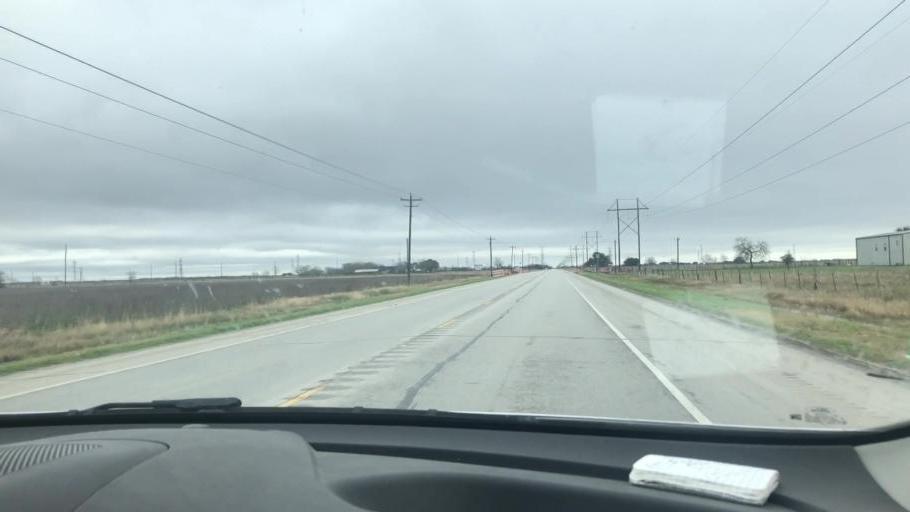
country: US
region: Texas
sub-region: Wharton County
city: Boling
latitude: 29.1875
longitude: -96.0124
